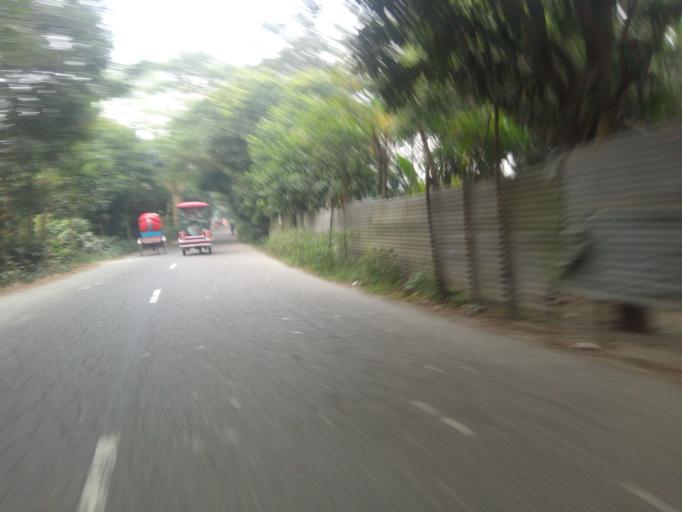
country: BD
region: Dhaka
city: Narayanganj
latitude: 23.5295
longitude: 90.4799
